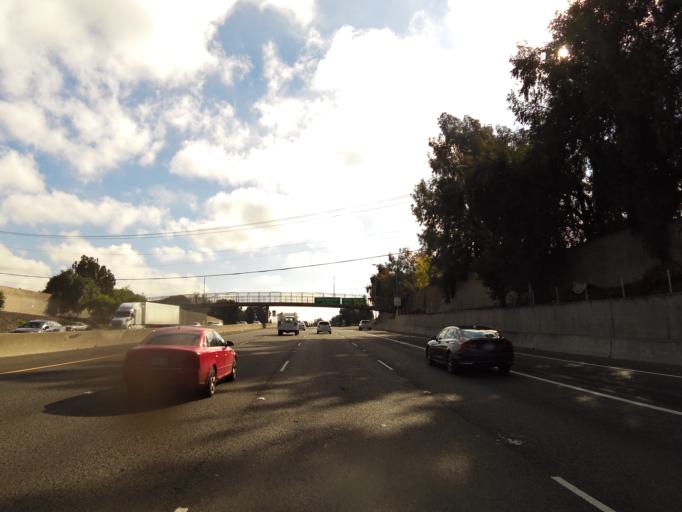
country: US
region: California
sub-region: Sacramento County
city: Parkway
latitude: 38.5146
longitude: -121.4623
